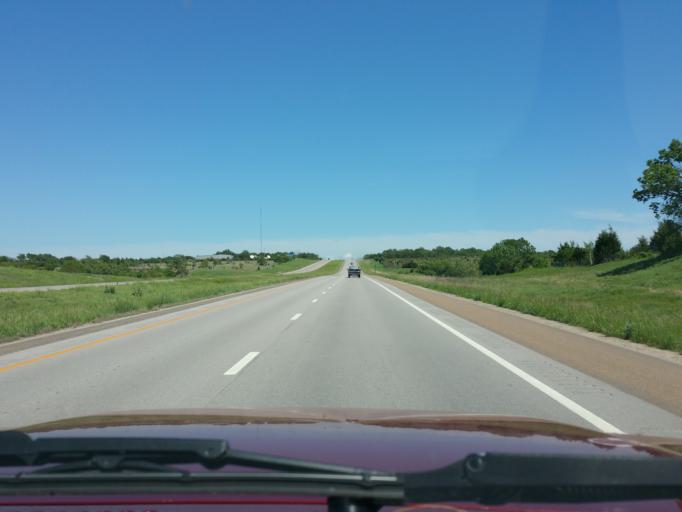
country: US
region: Kansas
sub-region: Pottawatomie County
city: Wamego
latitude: 39.2103
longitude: -96.3622
